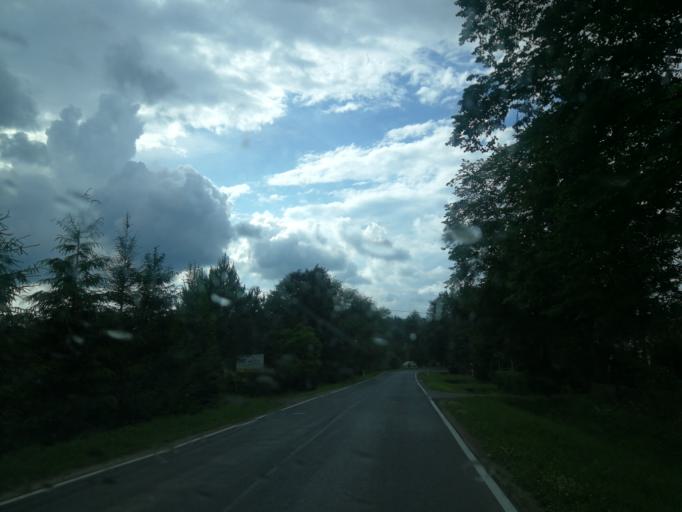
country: PL
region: Subcarpathian Voivodeship
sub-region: Powiat leski
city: Uherce Mineralne
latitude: 49.4603
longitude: 22.4025
